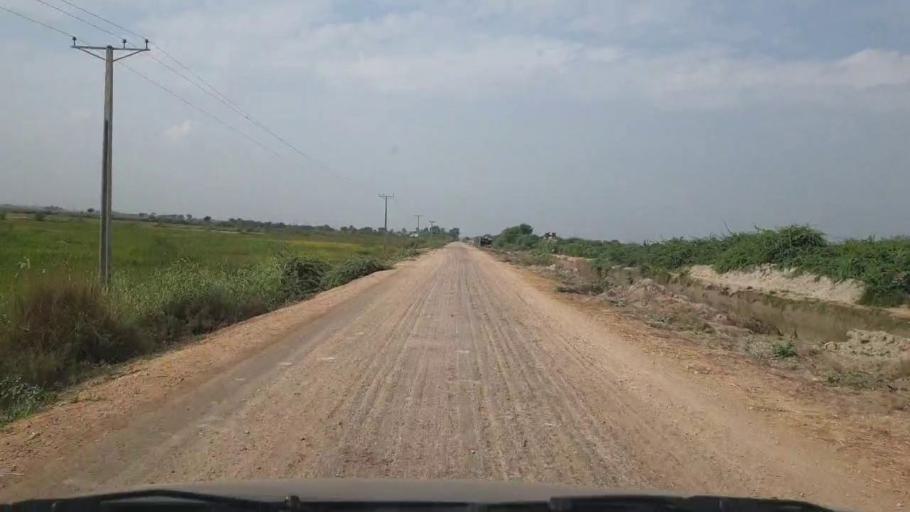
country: PK
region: Sindh
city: Kario
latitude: 24.6267
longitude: 68.5759
